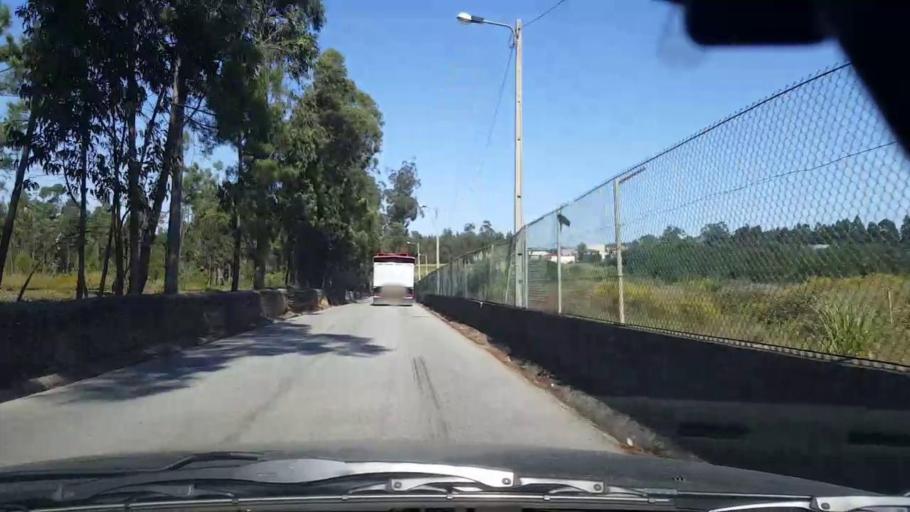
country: PT
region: Braga
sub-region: Vila Nova de Famalicao
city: Ribeirao
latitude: 41.3686
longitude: -8.6162
